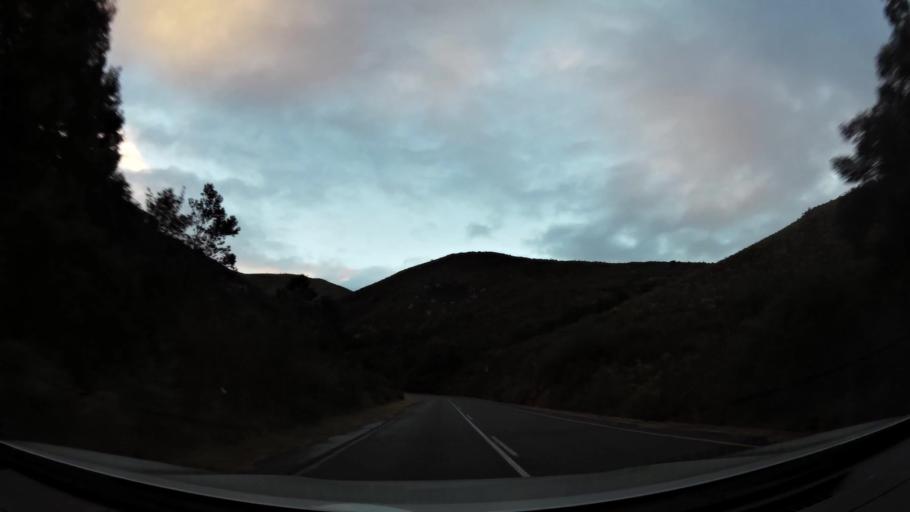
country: ZA
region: Western Cape
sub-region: Overberg District Municipality
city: Swellendam
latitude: -33.9863
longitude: 20.7191
